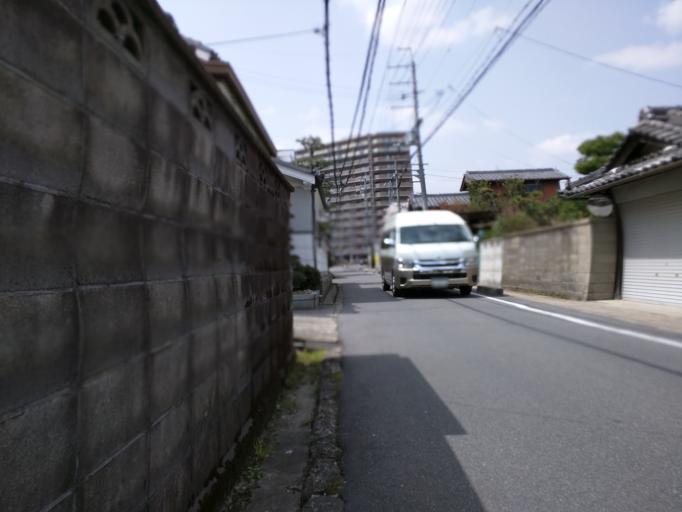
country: JP
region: Kyoto
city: Tanabe
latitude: 34.7982
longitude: 135.7888
